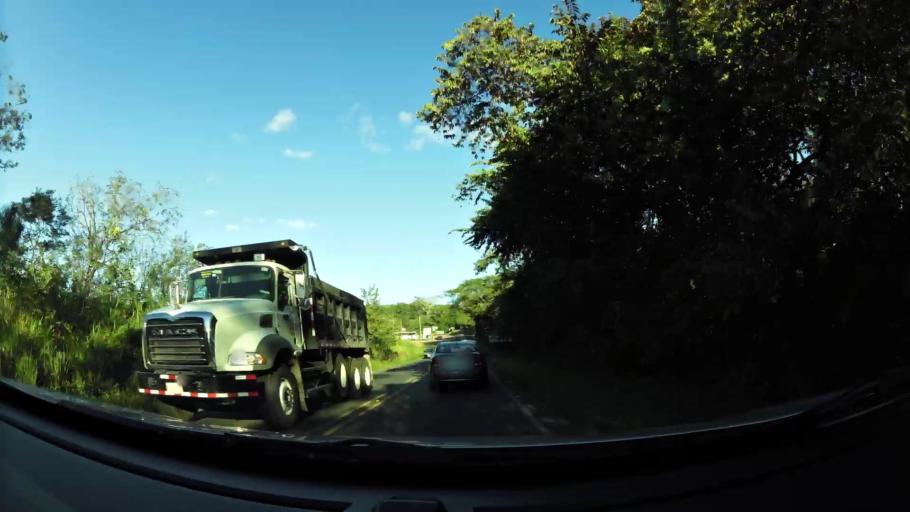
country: CR
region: Puntarenas
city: Miramar
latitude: 10.0899
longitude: -84.7948
